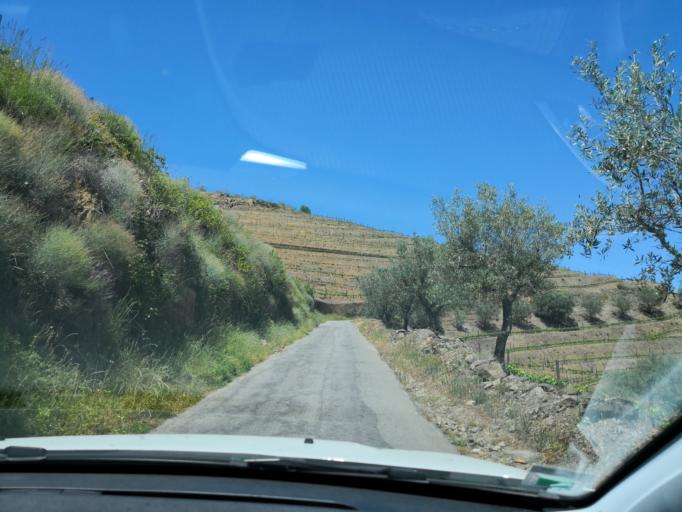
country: PT
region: Vila Real
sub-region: Vila Real
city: Vila Real
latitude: 41.2308
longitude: -7.7206
